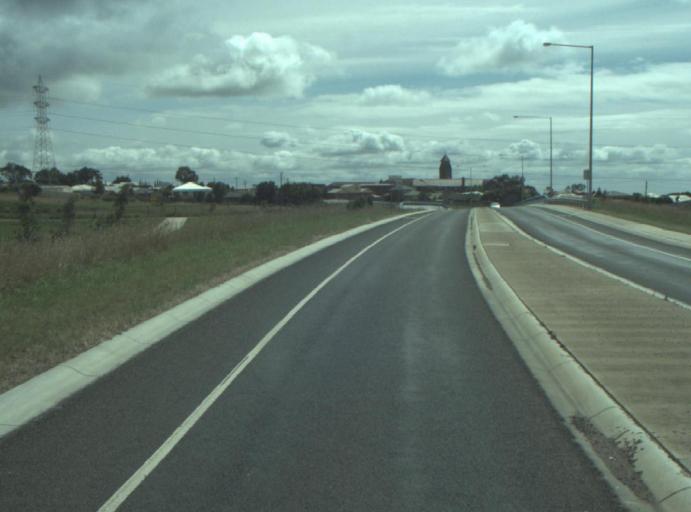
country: AU
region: Victoria
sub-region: Greater Geelong
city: Wandana Heights
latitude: -38.1902
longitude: 144.3068
